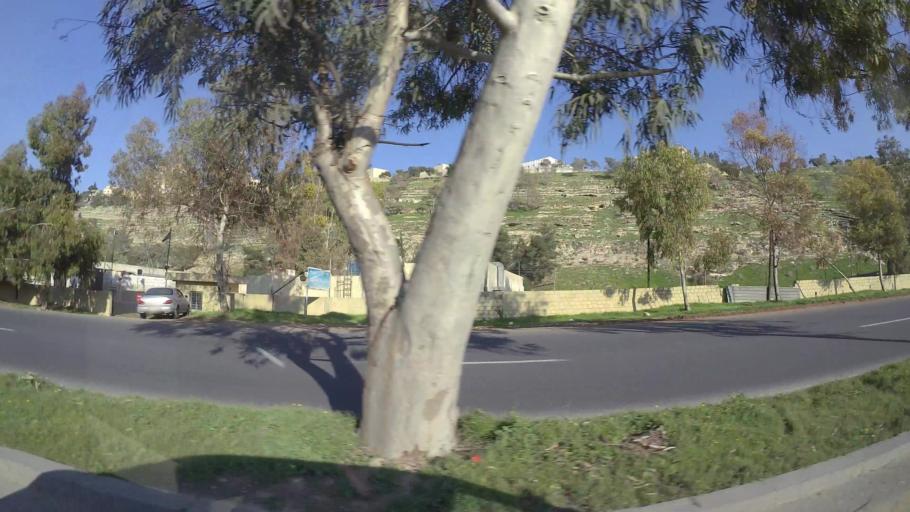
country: JO
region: Amman
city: Amman
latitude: 31.9746
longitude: 35.9719
